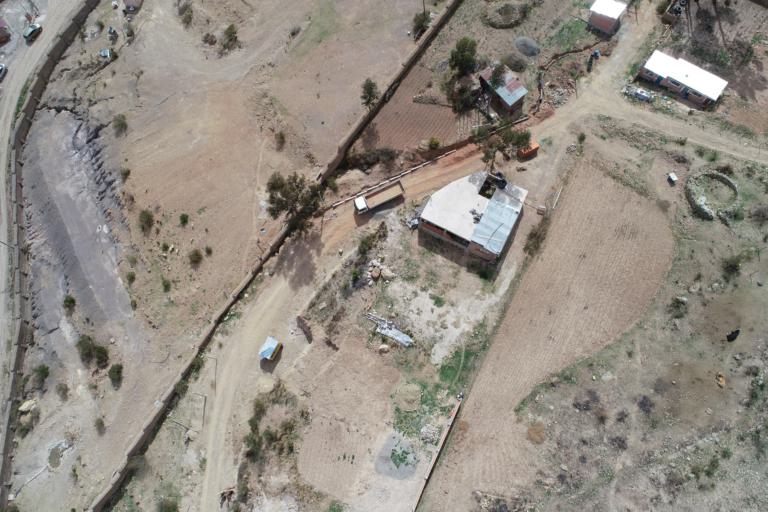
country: BO
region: La Paz
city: La Paz
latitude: -16.5538
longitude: -68.0521
